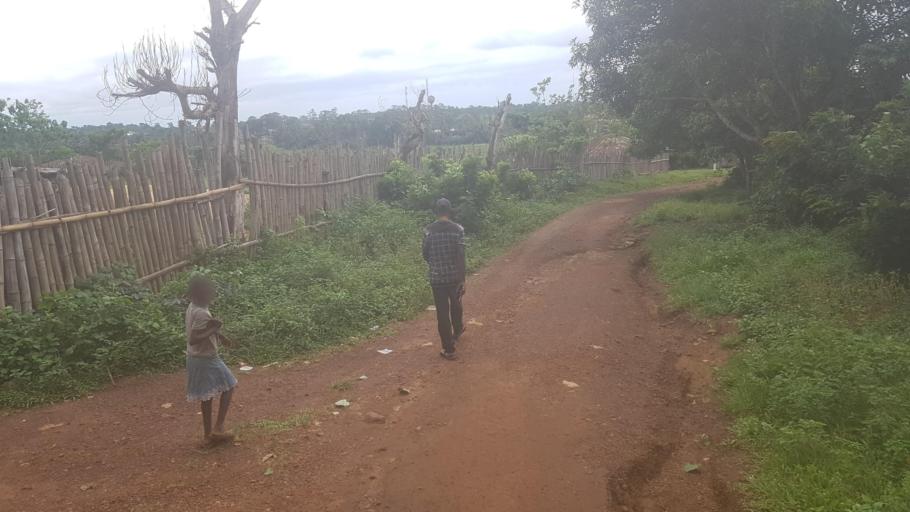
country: SL
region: Southern Province
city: Mogbwemo
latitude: 7.6123
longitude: -12.1755
